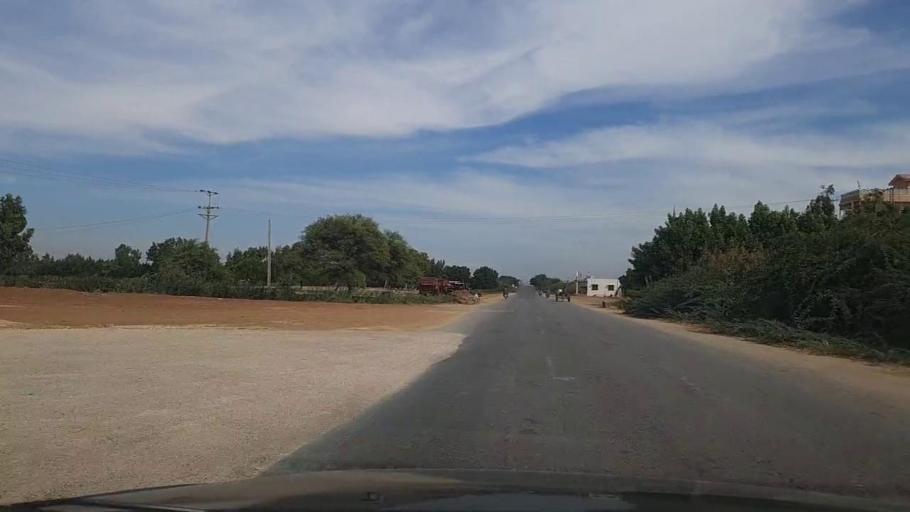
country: PK
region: Sindh
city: Thatta
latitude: 24.7886
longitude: 67.9544
